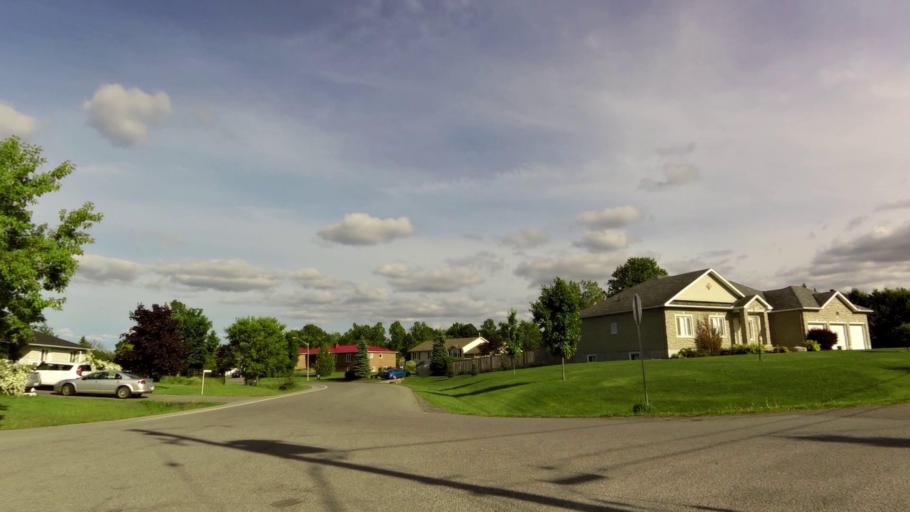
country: CA
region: Ontario
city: Ottawa
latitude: 45.2652
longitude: -75.5659
